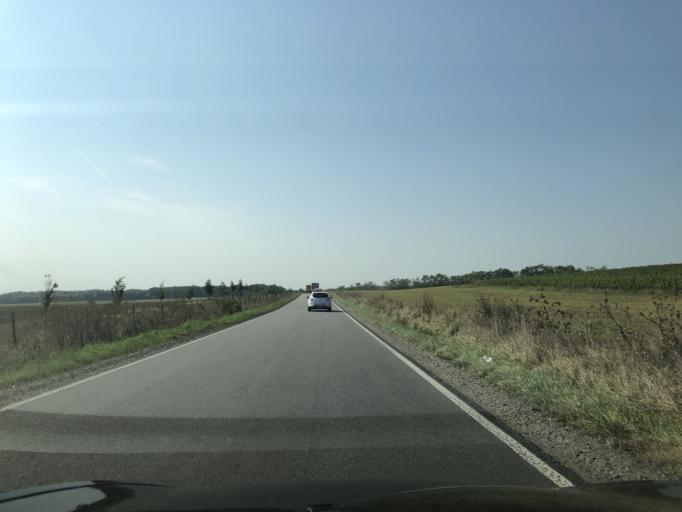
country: CZ
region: South Moravian
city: Drnholec
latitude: 48.8853
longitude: 16.5001
